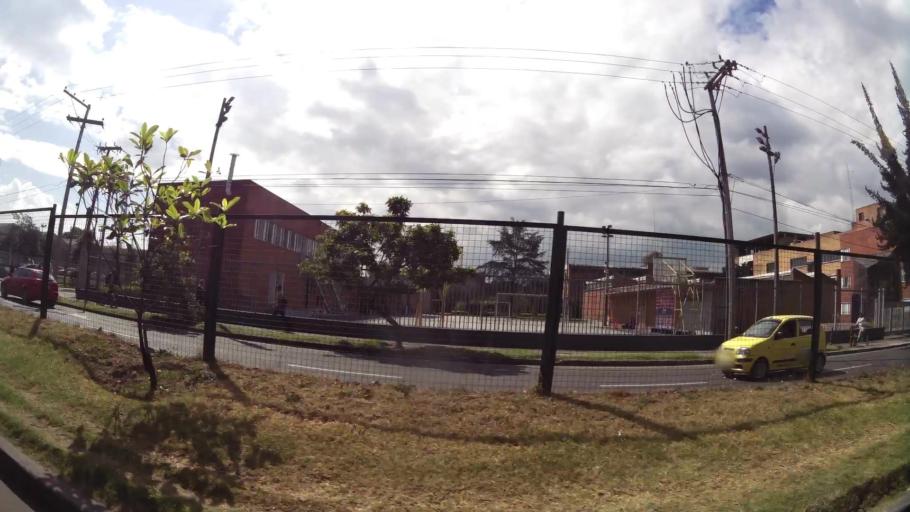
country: CO
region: Bogota D.C.
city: Bogota
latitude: 4.6311
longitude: -74.1175
